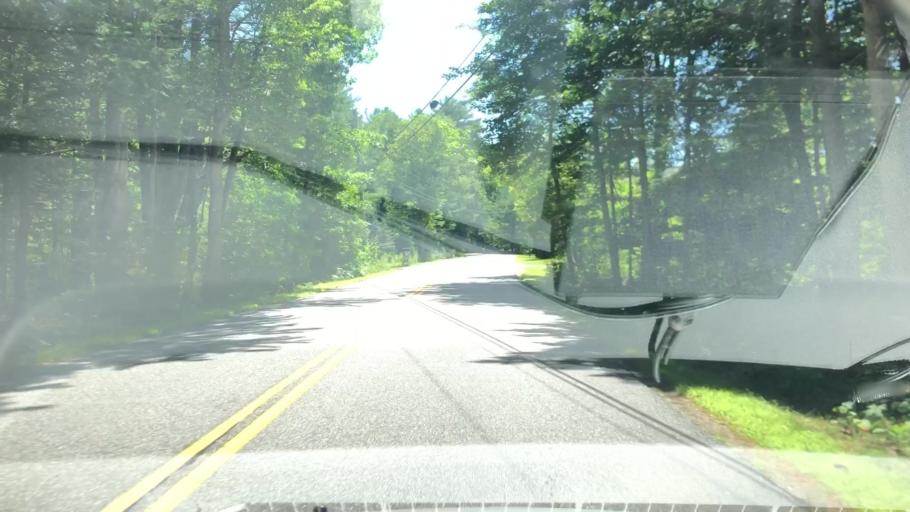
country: US
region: New Hampshire
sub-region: Hillsborough County
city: Milford
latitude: 42.8589
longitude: -71.5923
